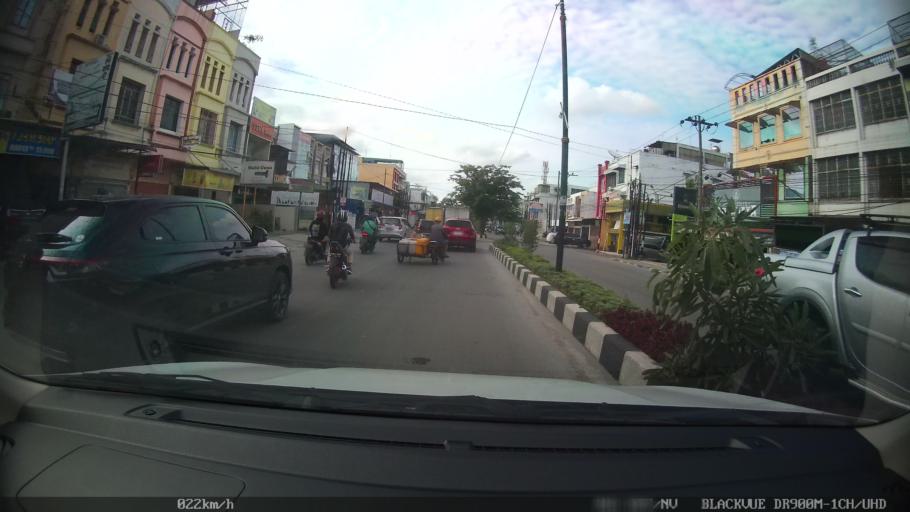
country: ID
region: North Sumatra
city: Medan
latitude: 3.6145
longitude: 98.6806
